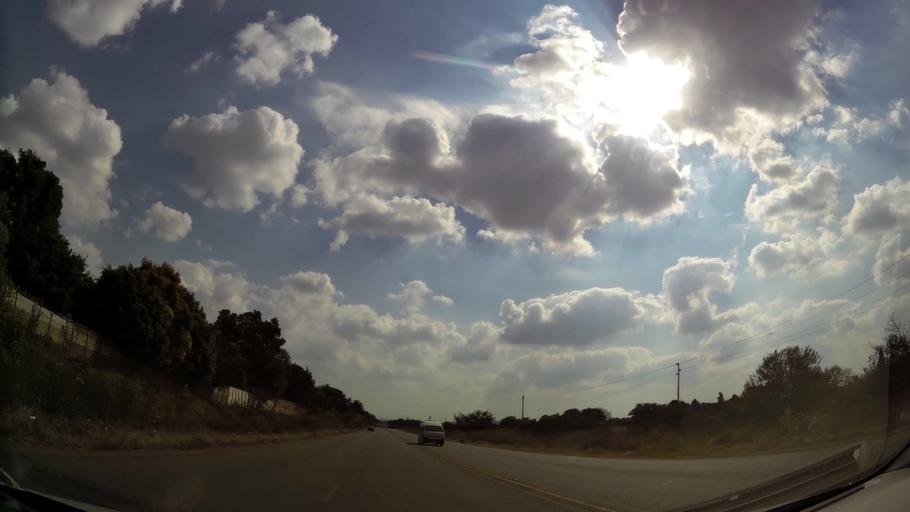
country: ZA
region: Gauteng
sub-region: City of Tshwane Metropolitan Municipality
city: Centurion
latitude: -25.8049
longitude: 28.3250
